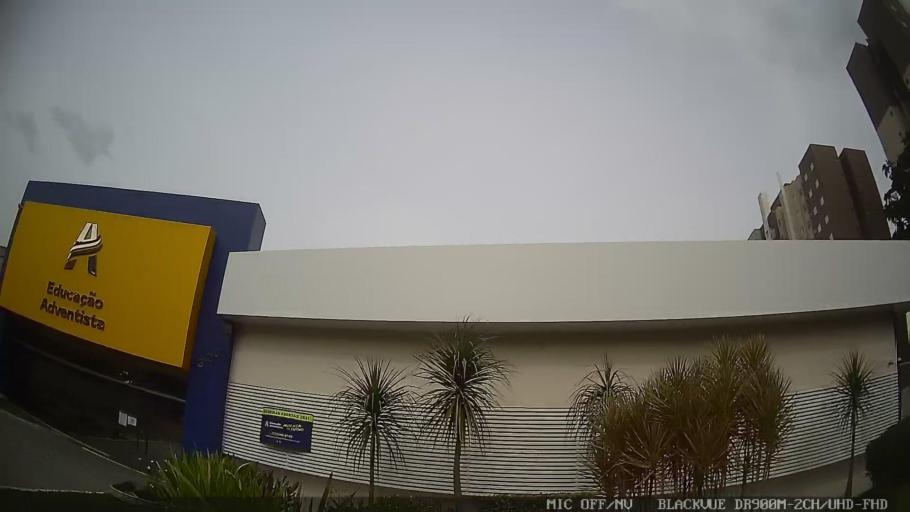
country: BR
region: Sao Paulo
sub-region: Indaiatuba
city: Indaiatuba
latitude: -23.0978
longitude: -47.1978
